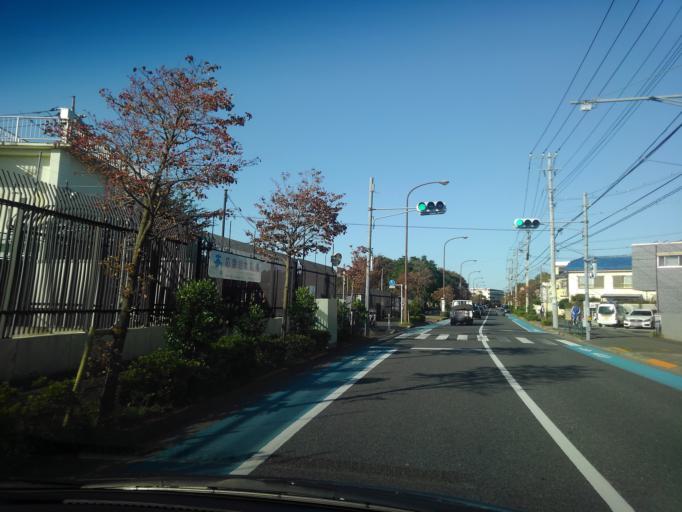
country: JP
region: Tokyo
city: Chofugaoka
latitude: 35.6614
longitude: 139.5323
